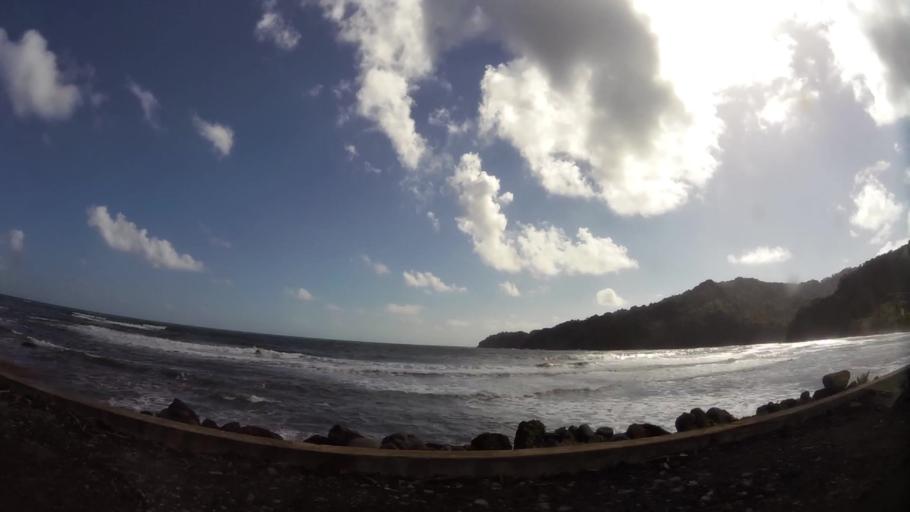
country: DM
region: Saint Andrew
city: Marigot
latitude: 15.5232
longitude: -61.2757
